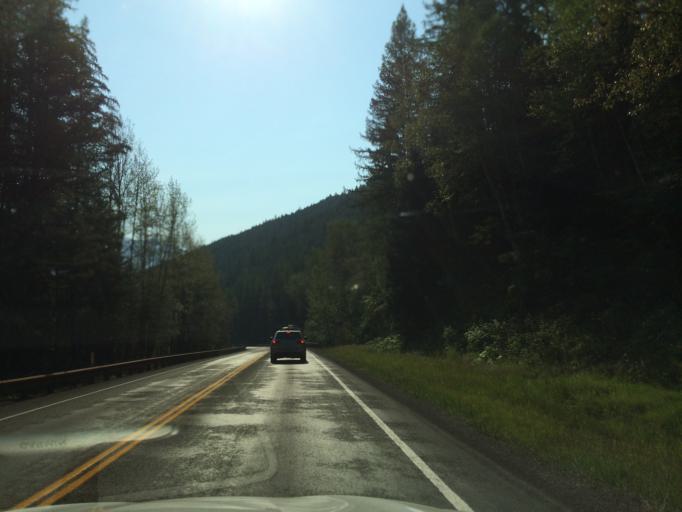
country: US
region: Montana
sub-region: Flathead County
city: Columbia Falls
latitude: 48.4903
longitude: -113.8744
